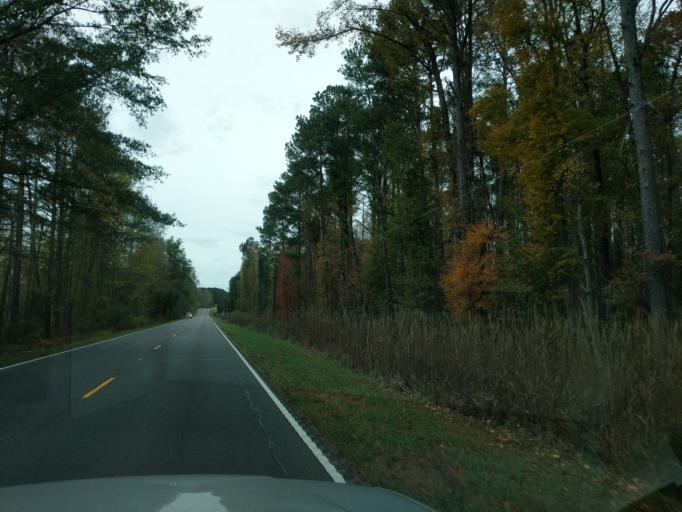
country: US
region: South Carolina
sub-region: Lexington County
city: Batesburg
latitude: 33.9303
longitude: -81.5960
